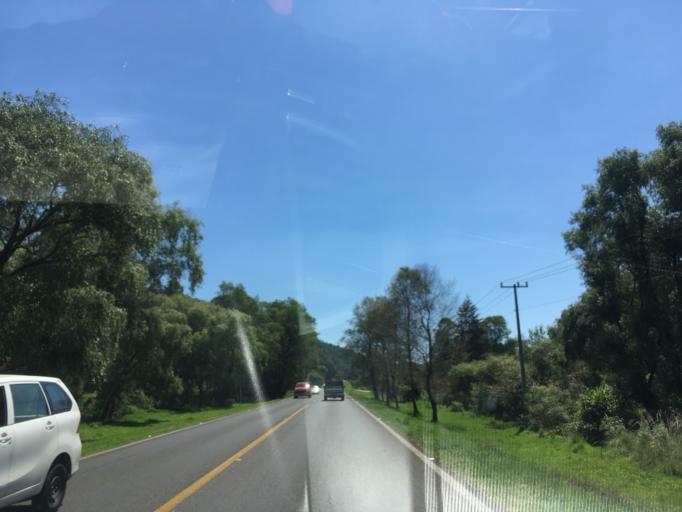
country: MX
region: Michoacan
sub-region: Hidalgo
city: San Lucas Huarirapeo (La Mesa de San Lucas)
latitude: 19.6739
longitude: -100.6632
